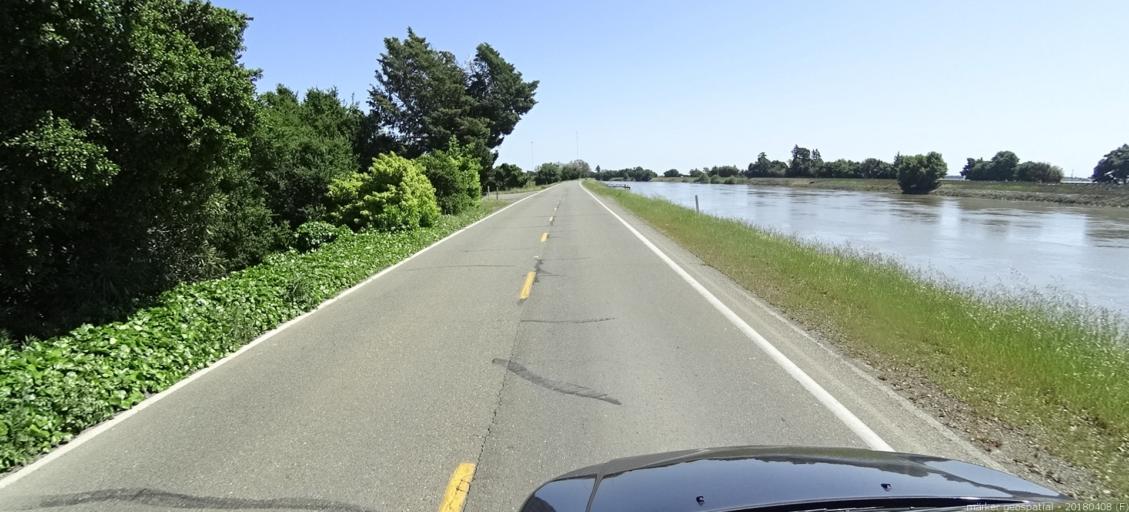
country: US
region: California
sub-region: Sacramento County
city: Walnut Grove
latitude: 38.2886
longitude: -121.5569
